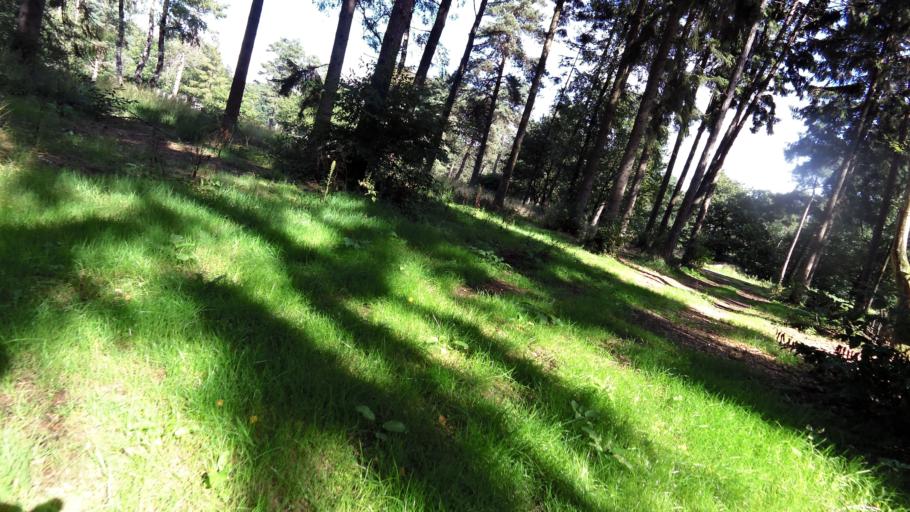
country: NL
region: Gelderland
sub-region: Gemeente Ede
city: Bennekom
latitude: 52.0128
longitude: 5.7135
